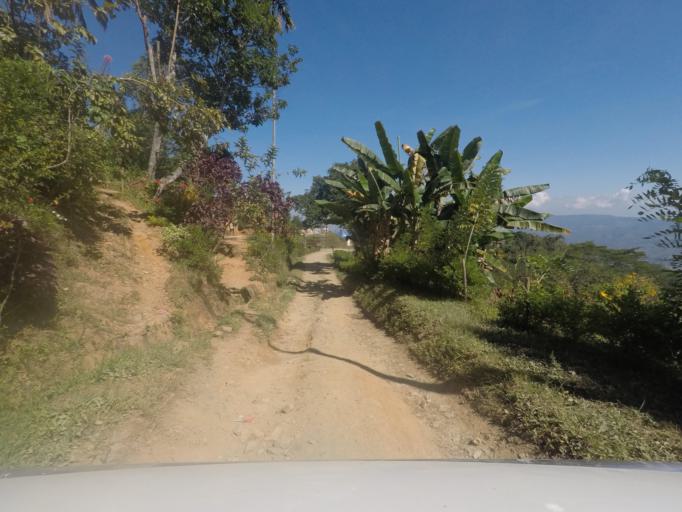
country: TL
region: Ermera
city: Gleno
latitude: -8.7235
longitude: 125.3280
